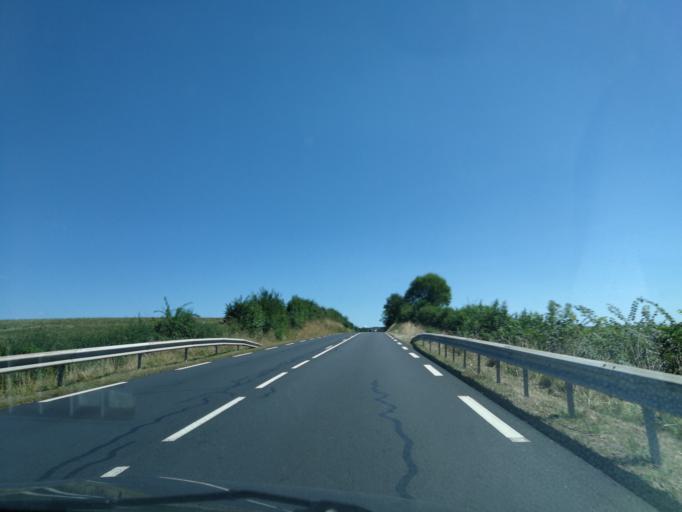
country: FR
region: Auvergne
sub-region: Departement du Cantal
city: Ytrac
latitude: 44.9335
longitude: 2.3650
